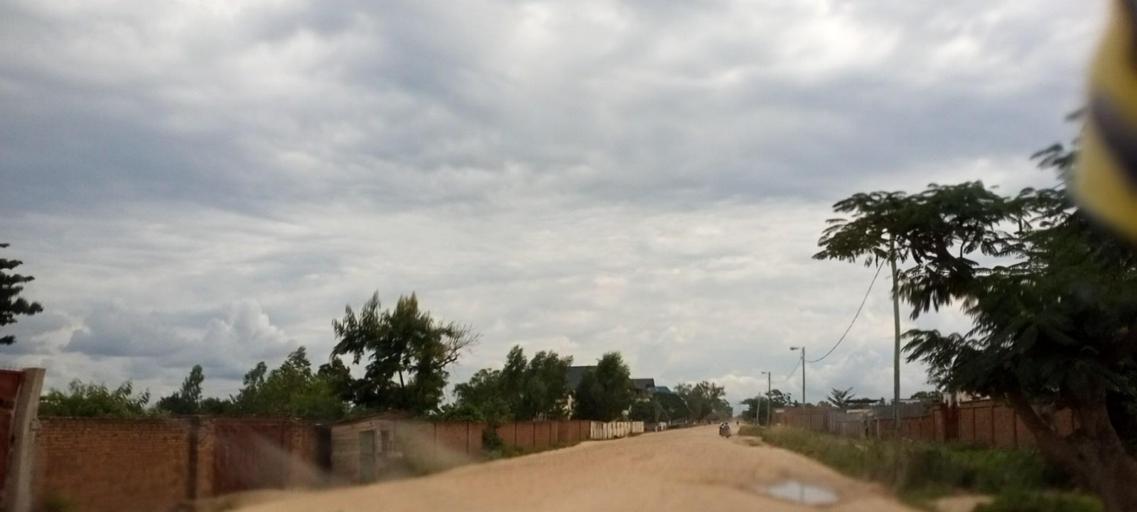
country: CD
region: South Kivu
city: Uvira
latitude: -3.3465
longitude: 29.1754
